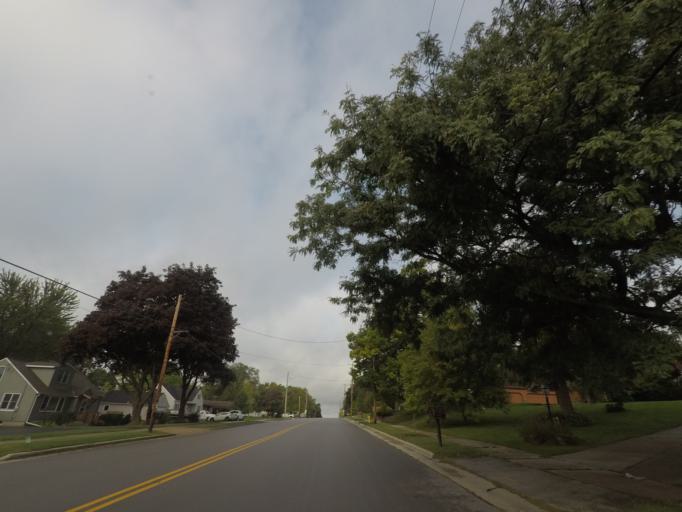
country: US
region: Wisconsin
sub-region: Waukesha County
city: Waukesha
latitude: 43.0321
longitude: -88.2594
